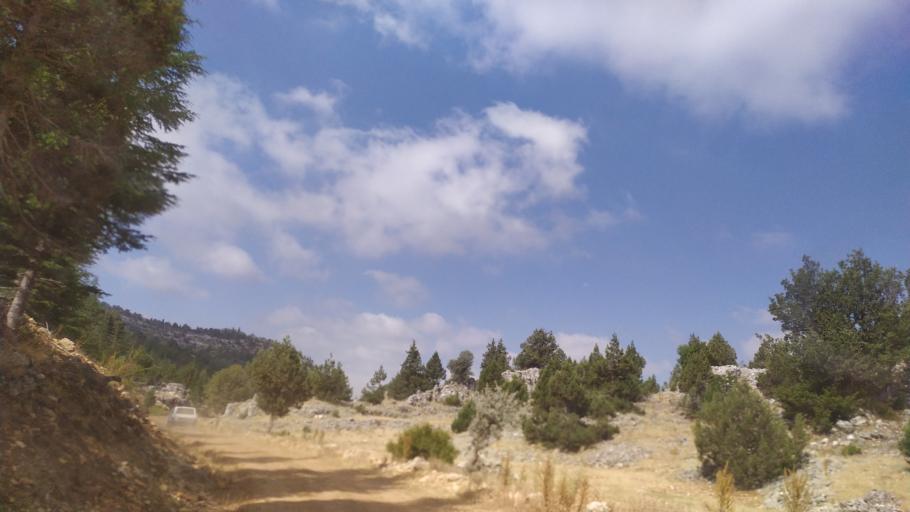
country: TR
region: Mersin
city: Kirobasi
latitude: 36.6197
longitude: 33.8392
